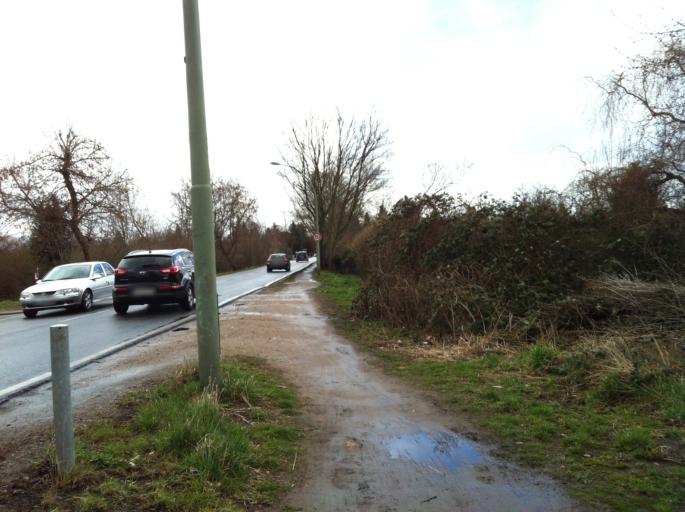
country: DE
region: Berlin
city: Karow
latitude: 52.6163
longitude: 13.4602
